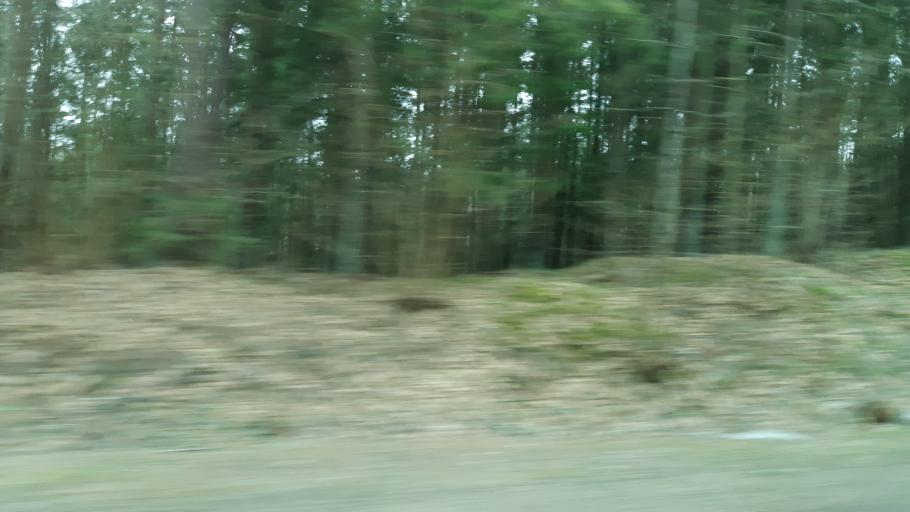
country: PL
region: Podlasie
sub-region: Suwalki
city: Suwalki
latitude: 54.2865
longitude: 22.9531
